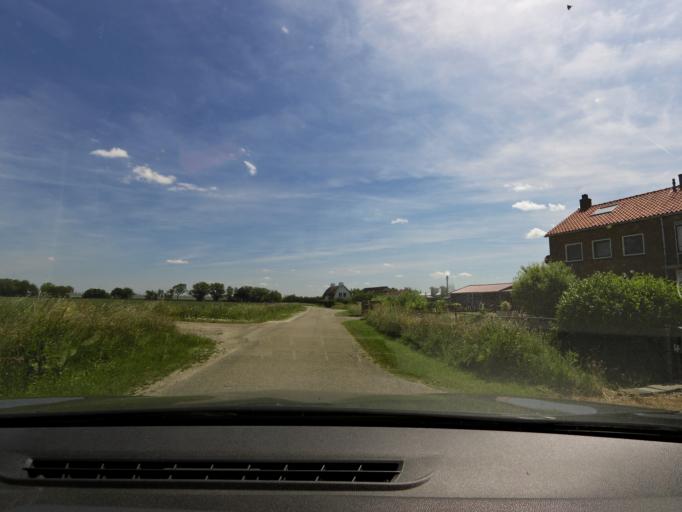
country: NL
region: South Holland
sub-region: Gemeente Brielle
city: Brielle
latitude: 51.9137
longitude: 4.1465
